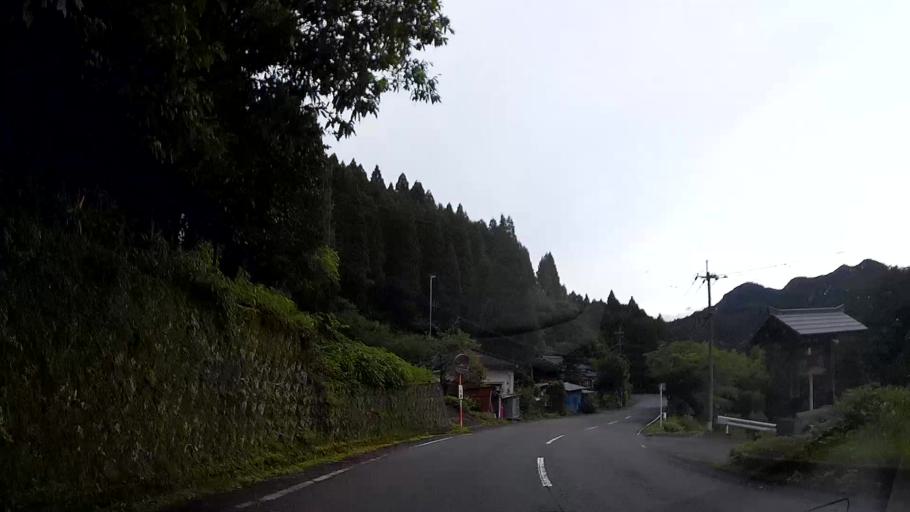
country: JP
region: Kumamoto
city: Kikuchi
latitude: 33.0932
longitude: 130.9556
